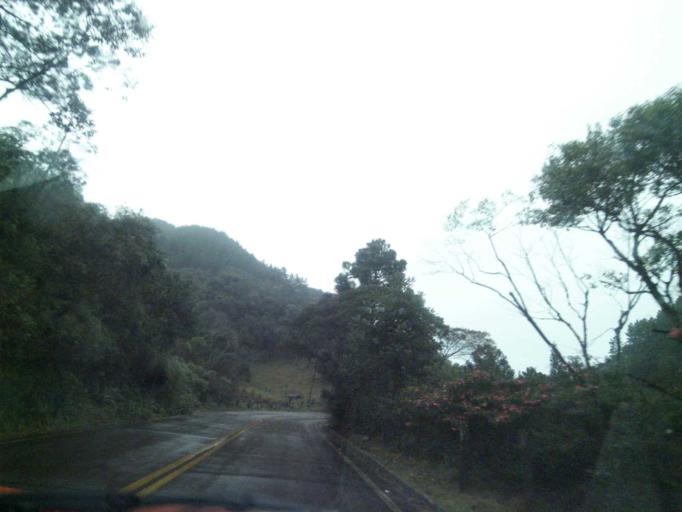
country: BR
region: Santa Catarina
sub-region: Anitapolis
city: Anitapolis
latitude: -27.8000
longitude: -49.0456
